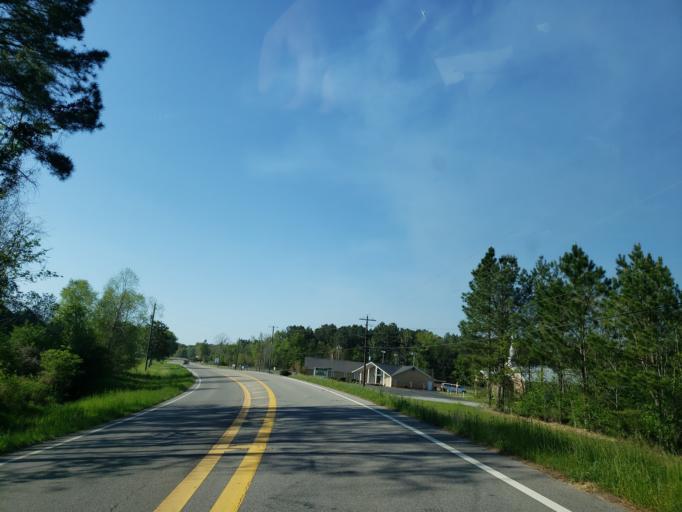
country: US
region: Mississippi
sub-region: Perry County
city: Richton
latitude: 31.3335
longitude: -88.9321
